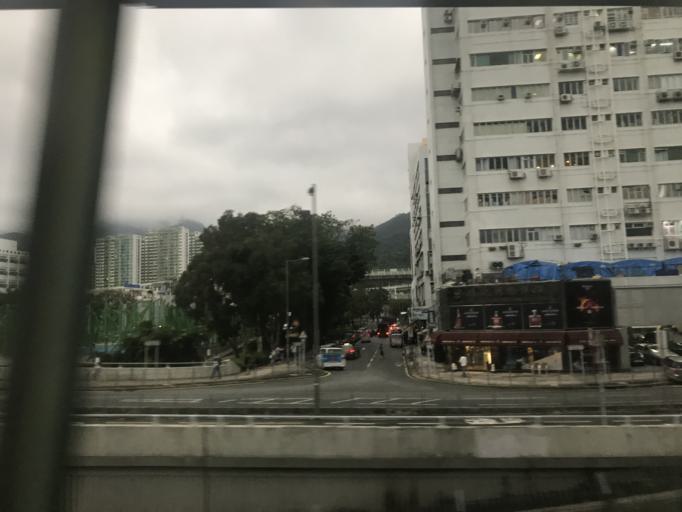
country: HK
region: Sha Tin
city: Sha Tin
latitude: 22.3751
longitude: 114.1812
